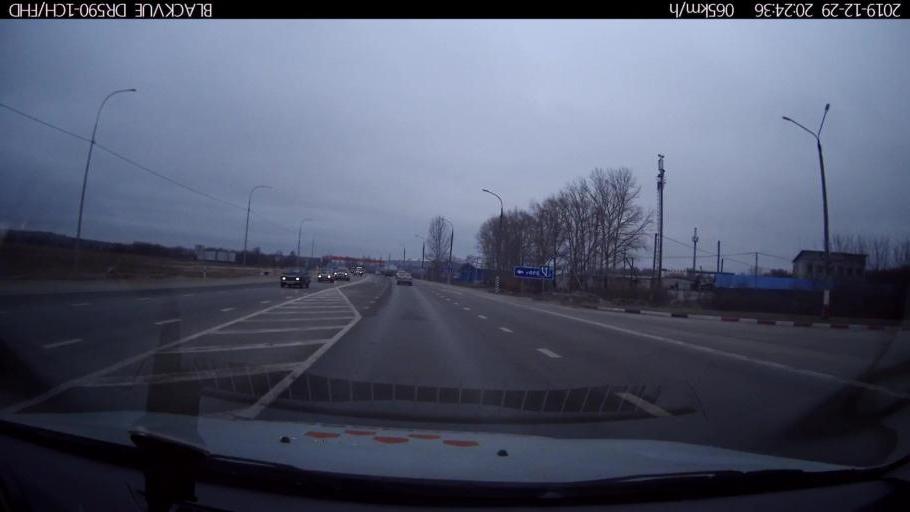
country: RU
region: Nizjnij Novgorod
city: Afonino
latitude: 56.2132
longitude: 44.1064
